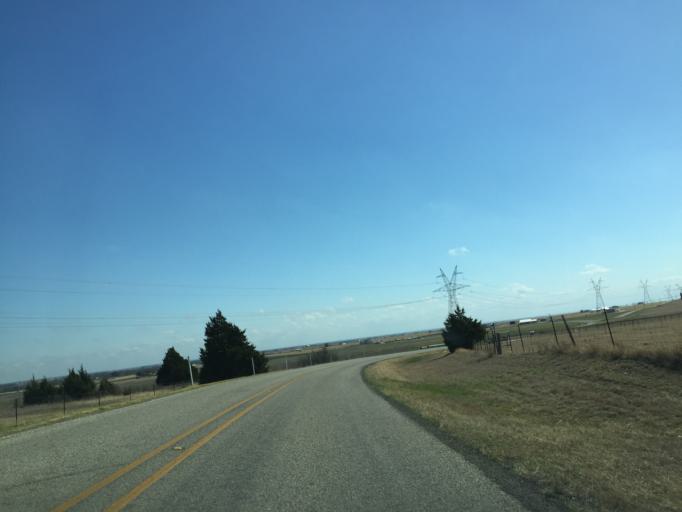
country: US
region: Texas
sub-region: Williamson County
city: Granger
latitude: 30.7582
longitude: -97.5259
